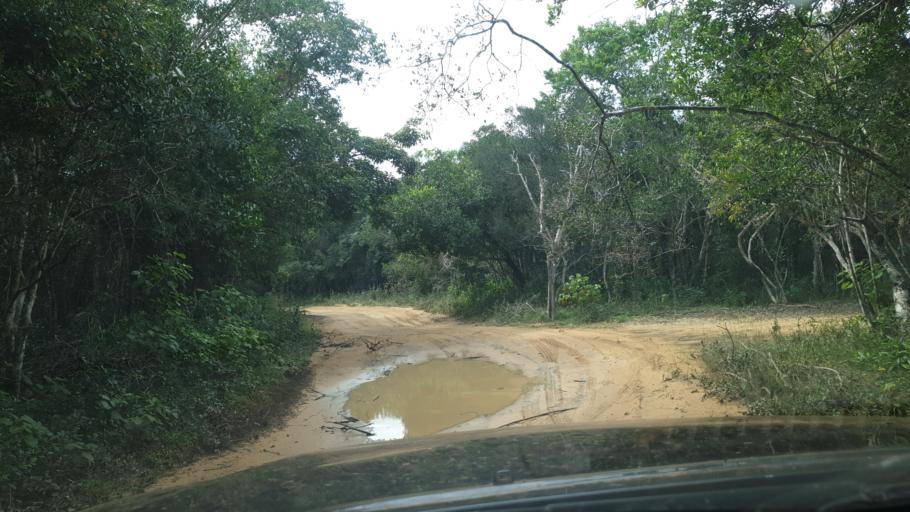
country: LK
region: North Western
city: Puttalam
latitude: 8.4185
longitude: 80.0023
